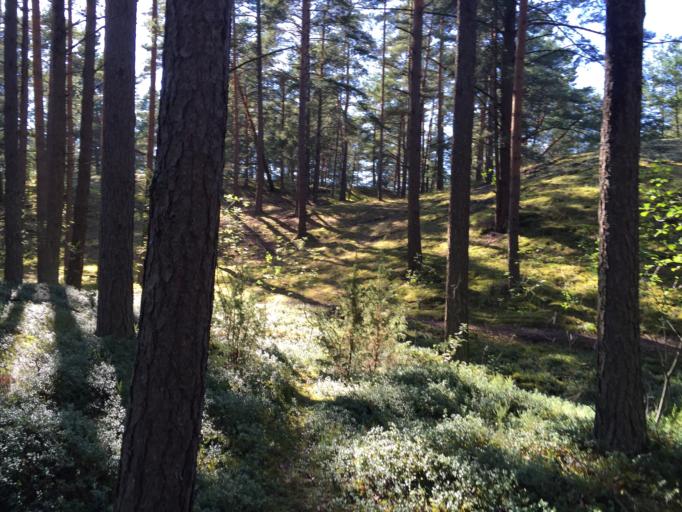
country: LV
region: Riga
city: Jaunciems
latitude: 57.0825
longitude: 24.1393
